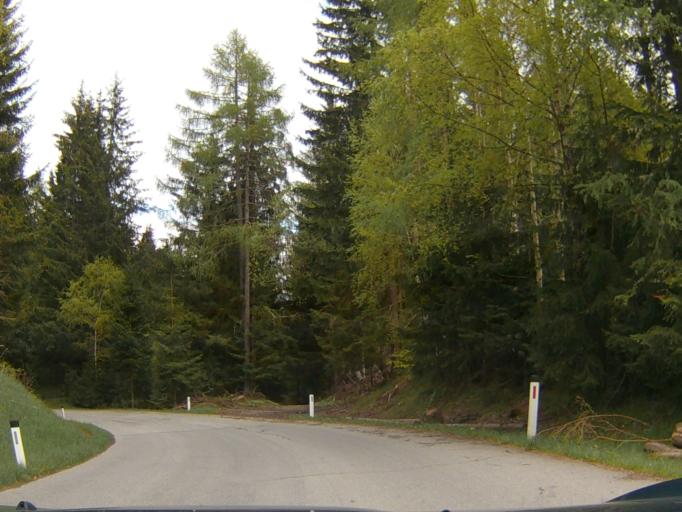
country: AT
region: Carinthia
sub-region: Politischer Bezirk Villach Land
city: Stockenboi
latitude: 46.7395
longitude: 13.5460
